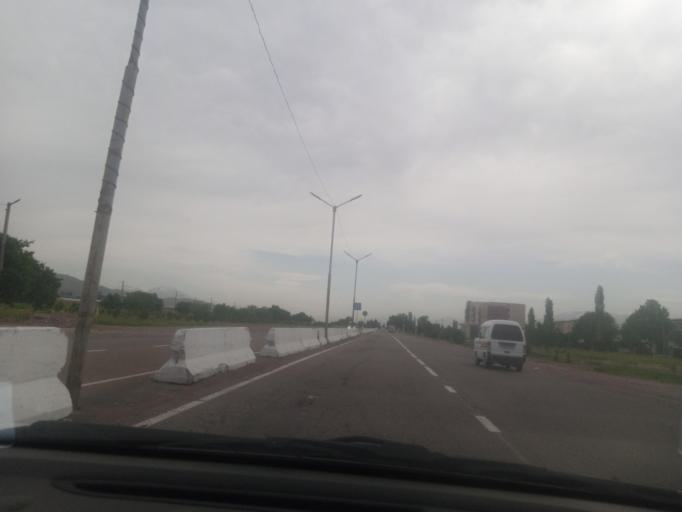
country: UZ
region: Toshkent
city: Ohangaron
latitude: 40.9088
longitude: 69.8047
